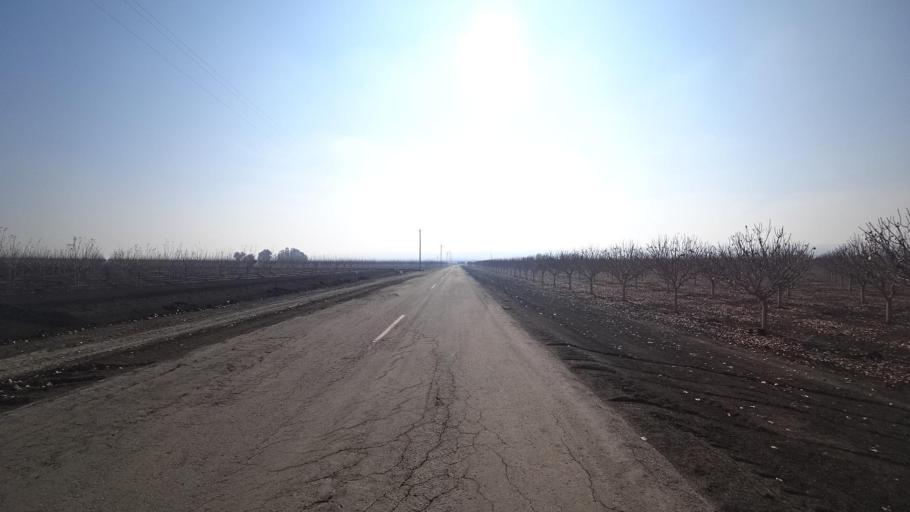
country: US
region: California
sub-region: Kern County
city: Buttonwillow
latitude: 35.3448
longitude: -119.4293
